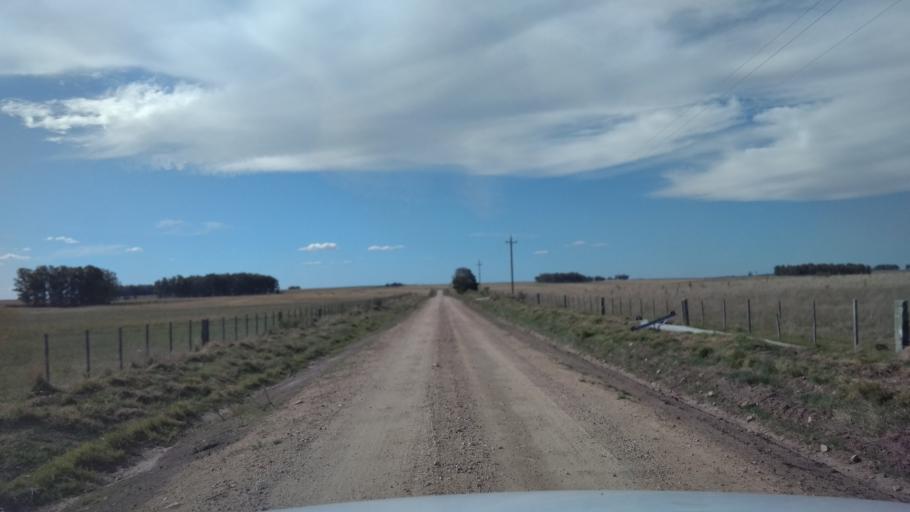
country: UY
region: Florida
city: Casupa
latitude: -34.0313
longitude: -55.7808
